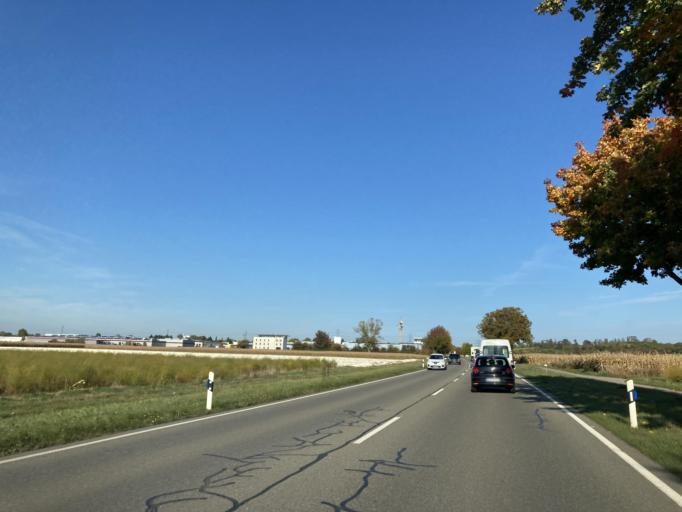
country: DE
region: Baden-Wuerttemberg
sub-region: Freiburg Region
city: Heitersheim
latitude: 47.8648
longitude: 7.6448
